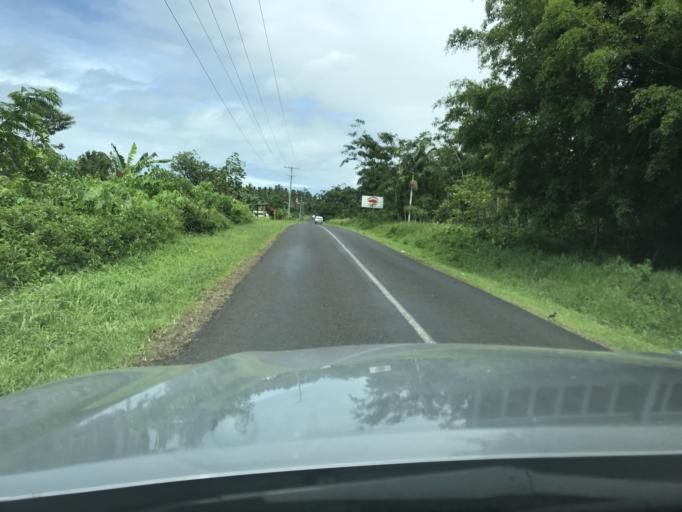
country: WS
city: Nofoali`i
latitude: -13.8738
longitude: -171.9252
